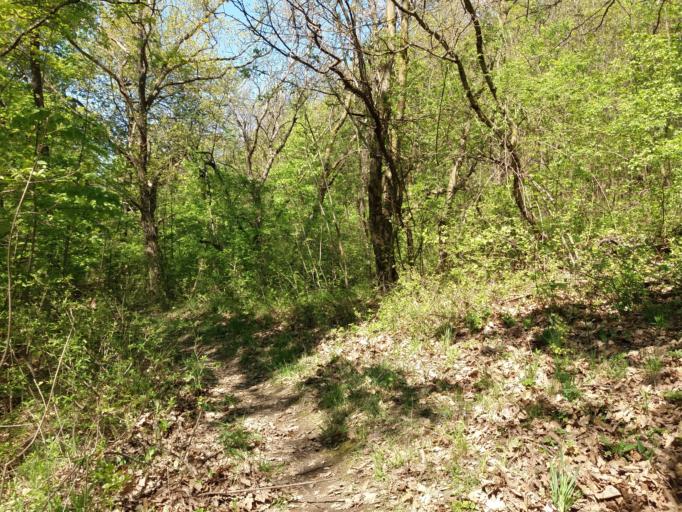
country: HU
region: Pest
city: Pilisszentkereszt
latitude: 47.6959
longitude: 18.9139
